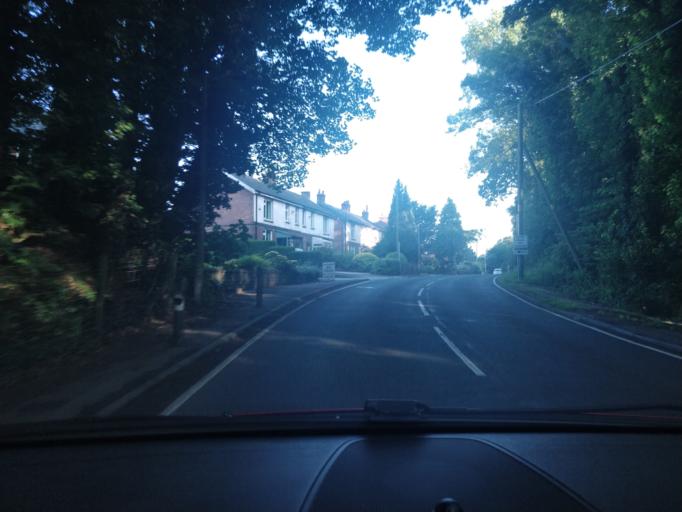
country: GB
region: England
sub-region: Lancashire
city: Banks
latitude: 53.6555
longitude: -2.8785
